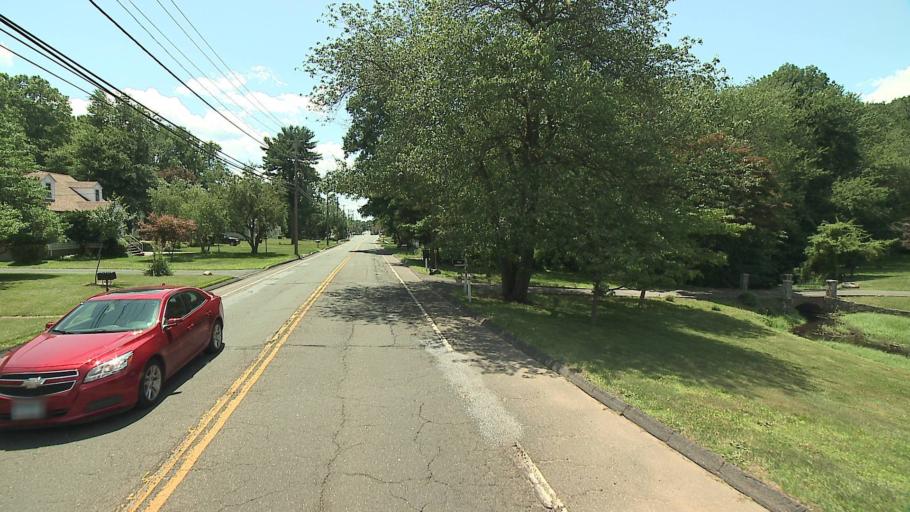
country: US
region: Connecticut
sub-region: Fairfield County
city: Trumbull
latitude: 41.2239
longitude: -73.1673
